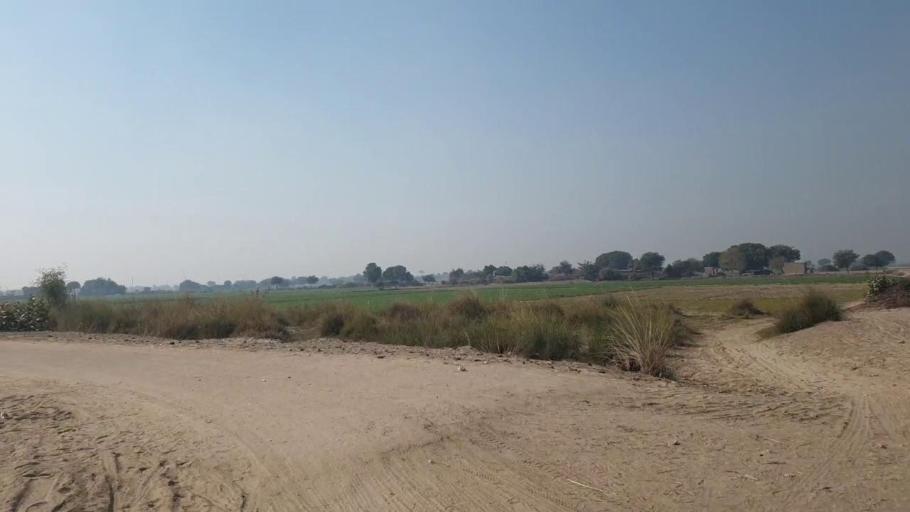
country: PK
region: Sindh
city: Shahpur Chakar
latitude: 26.1095
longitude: 68.6009
